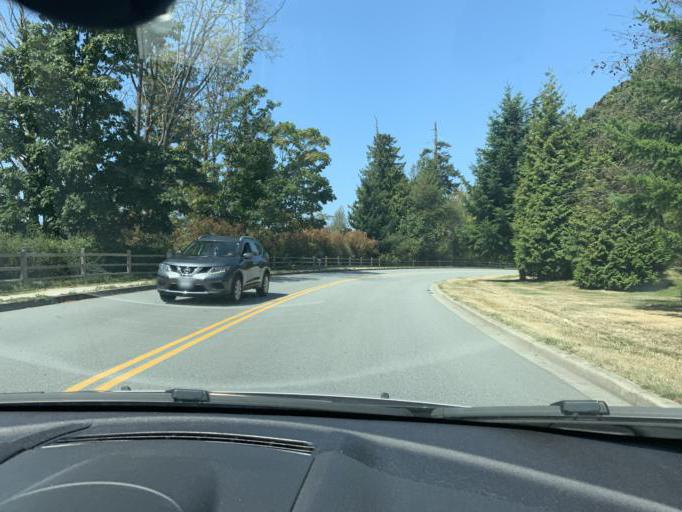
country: CA
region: British Columbia
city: West End
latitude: 49.2603
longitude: -123.2568
